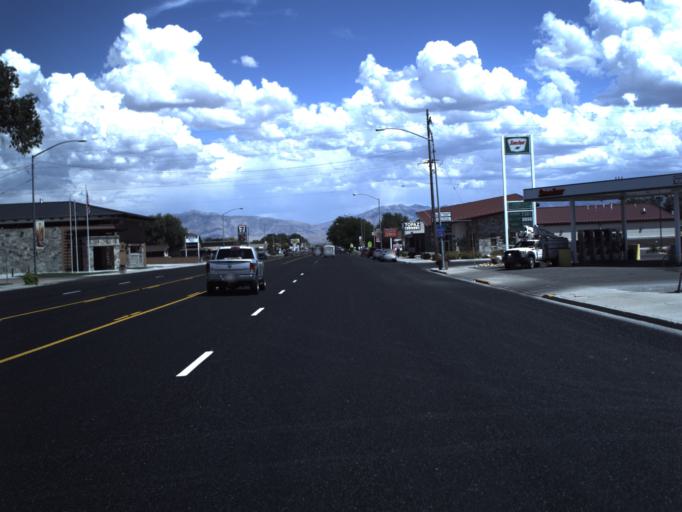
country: US
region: Utah
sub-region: Millard County
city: Delta
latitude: 39.3523
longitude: -112.5781
